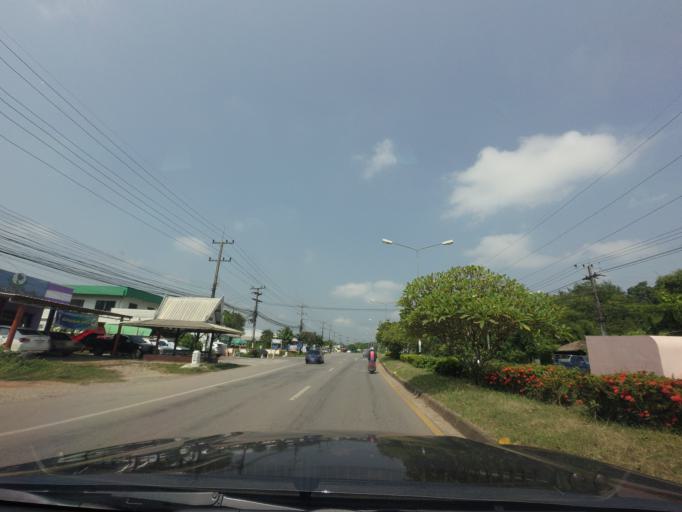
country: TH
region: Nan
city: Nan
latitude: 18.7866
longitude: 100.7425
